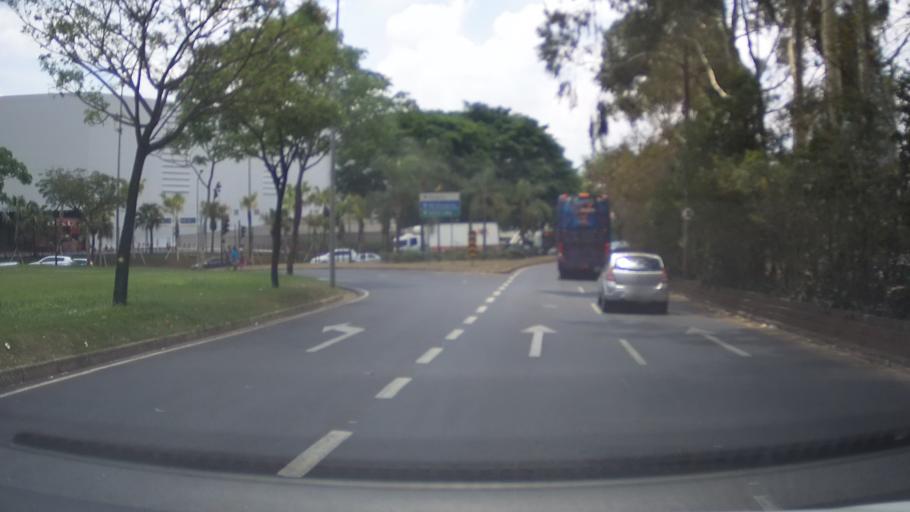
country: BR
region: Minas Gerais
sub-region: Belo Horizonte
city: Belo Horizonte
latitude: -19.9743
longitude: -43.9428
